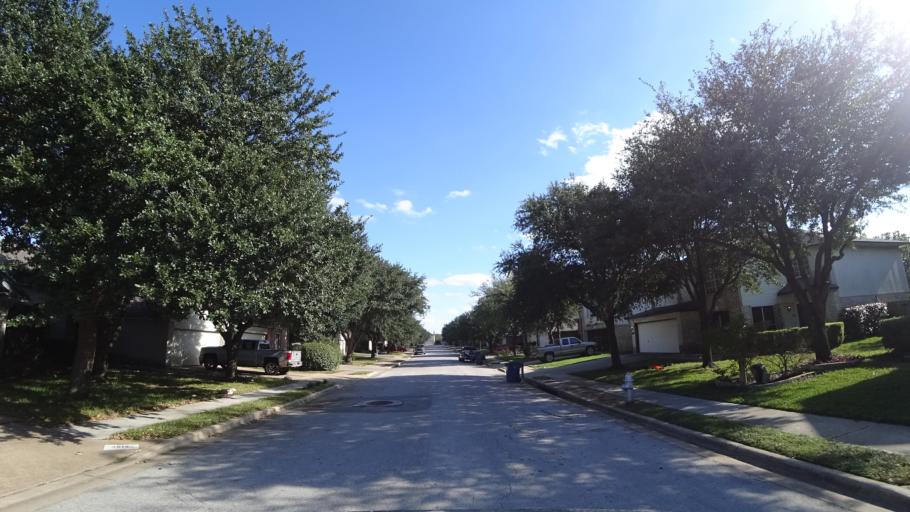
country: US
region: Texas
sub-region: Travis County
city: Wells Branch
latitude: 30.4607
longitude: -97.6832
